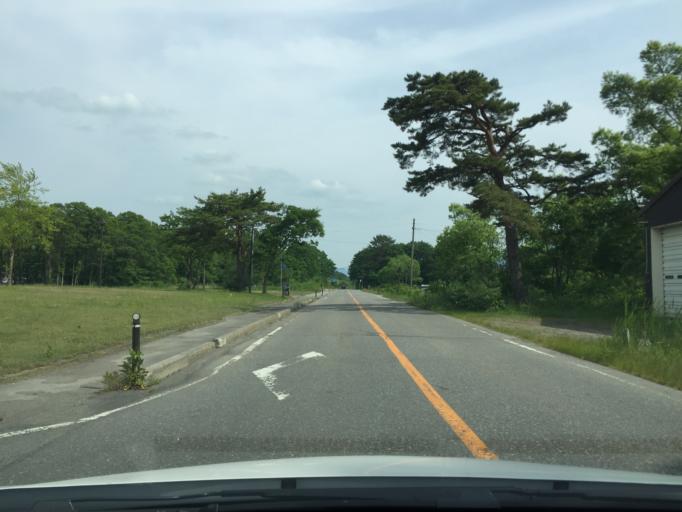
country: JP
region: Fukushima
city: Inawashiro
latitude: 37.6793
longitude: 140.0710
